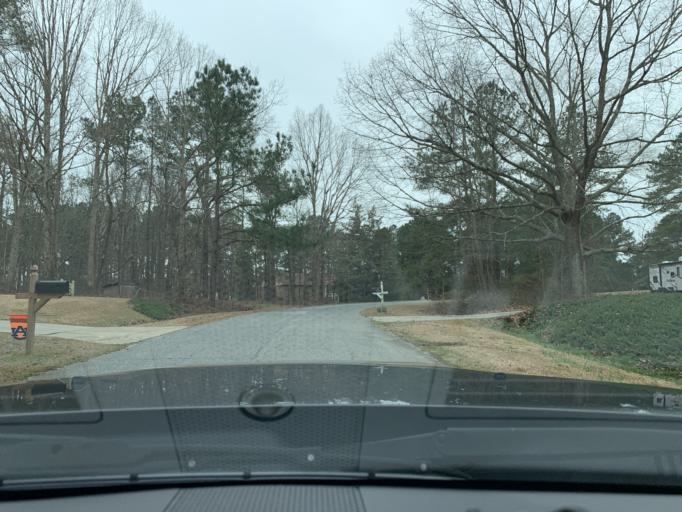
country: US
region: North Carolina
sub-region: Johnston County
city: Wilsons Mills
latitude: 35.6212
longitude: -78.3922
